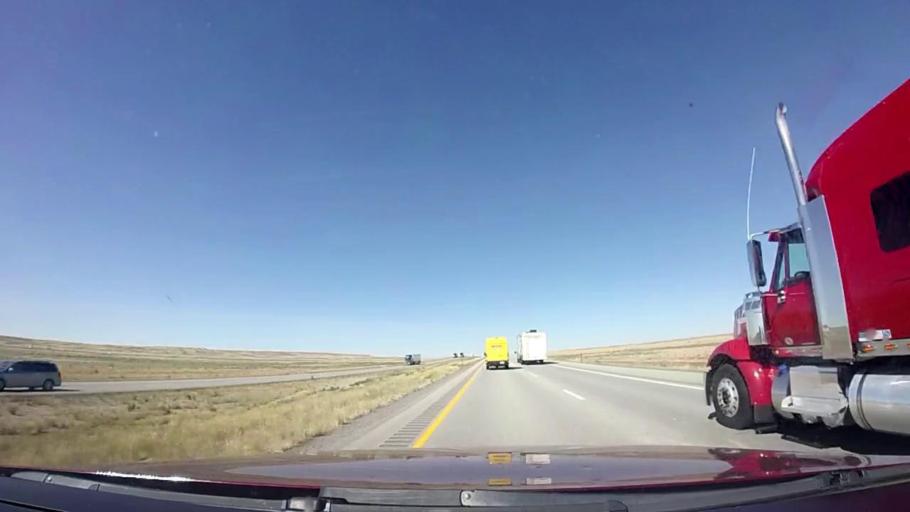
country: US
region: Wyoming
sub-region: Carbon County
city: Rawlins
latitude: 41.6620
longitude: -108.0583
